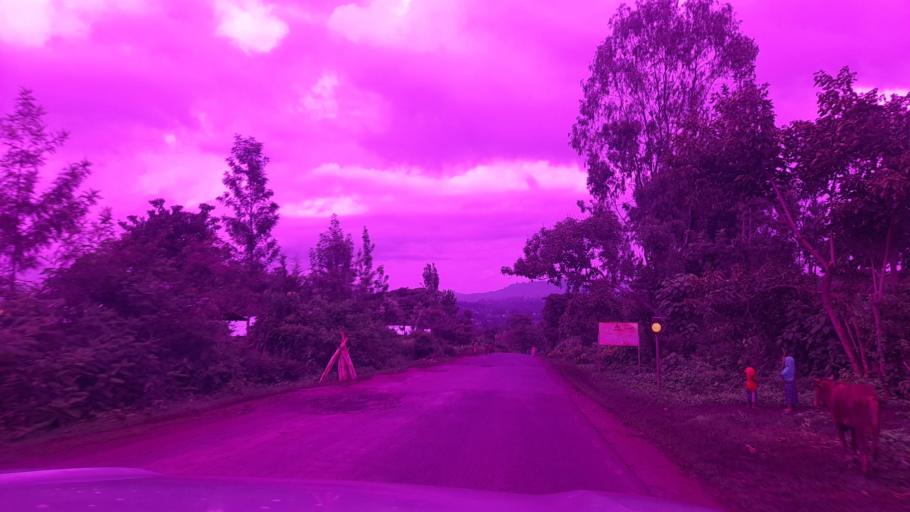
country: ET
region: Oromiya
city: Jima
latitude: 7.9153
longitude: 37.4015
